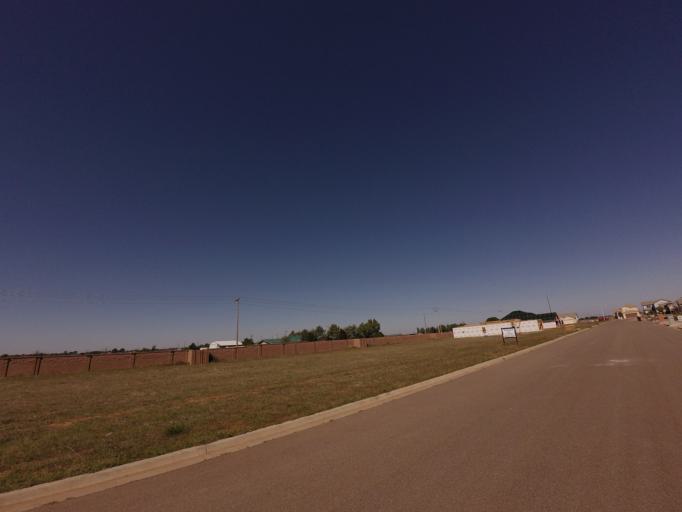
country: US
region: New Mexico
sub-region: Curry County
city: Clovis
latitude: 34.4243
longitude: -103.1601
